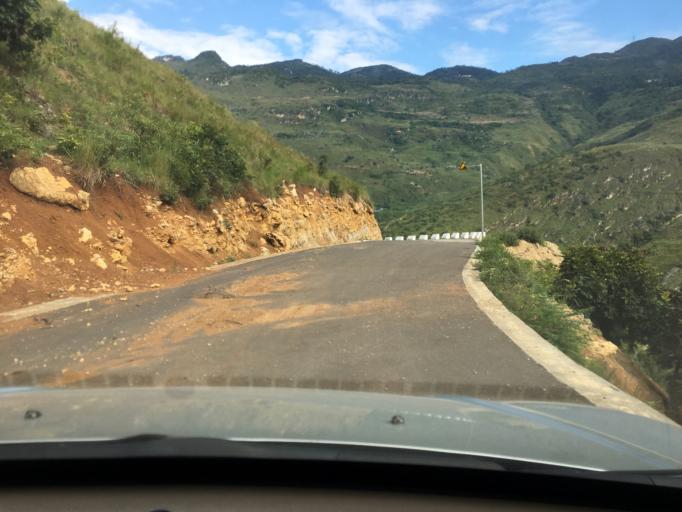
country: CN
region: Guizhou Sheng
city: Anshun
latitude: 25.7779
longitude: 105.3864
